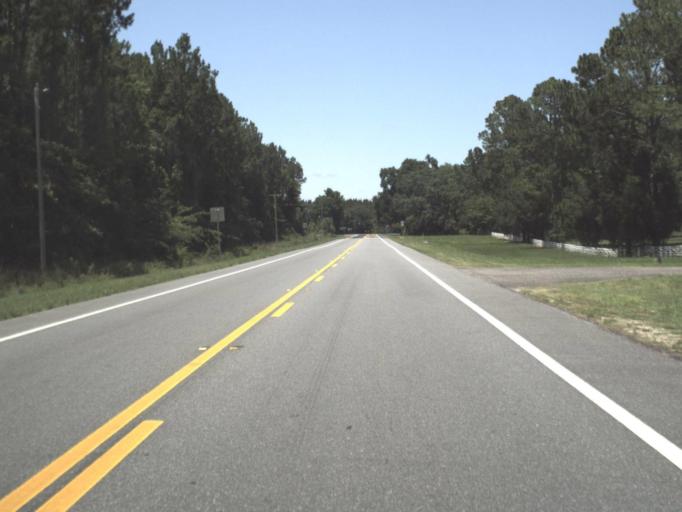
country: US
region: Florida
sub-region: Lafayette County
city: Mayo
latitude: 29.9456
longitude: -82.9488
